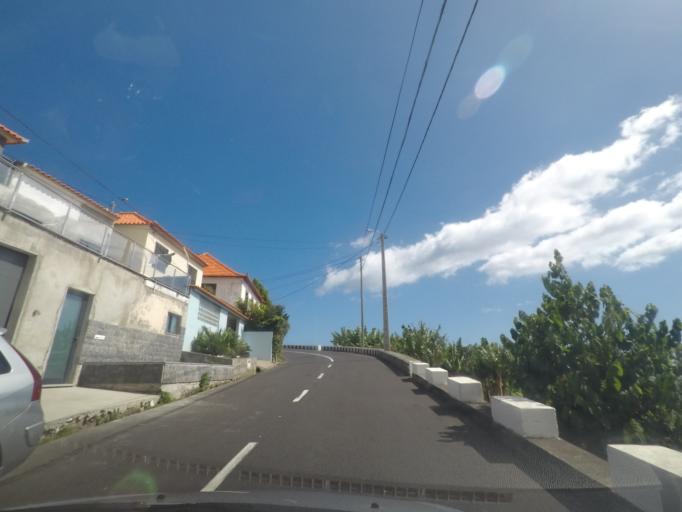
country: PT
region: Madeira
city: Ribeira Brava
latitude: 32.6696
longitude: -17.0580
